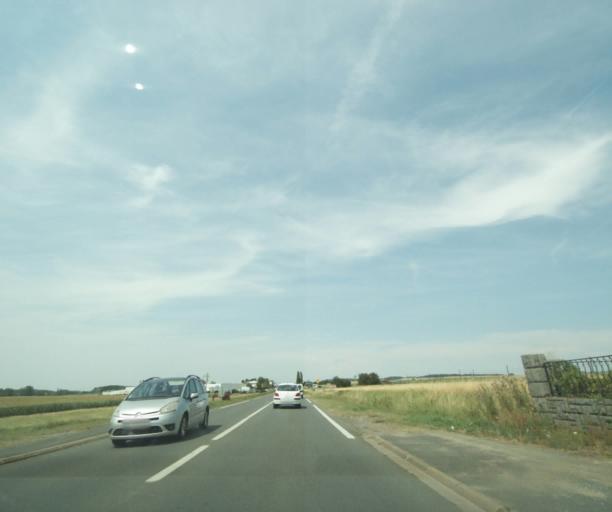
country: FR
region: Poitou-Charentes
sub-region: Departement de la Vienne
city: Dange-Saint-Romain
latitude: 46.9431
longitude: 0.6073
